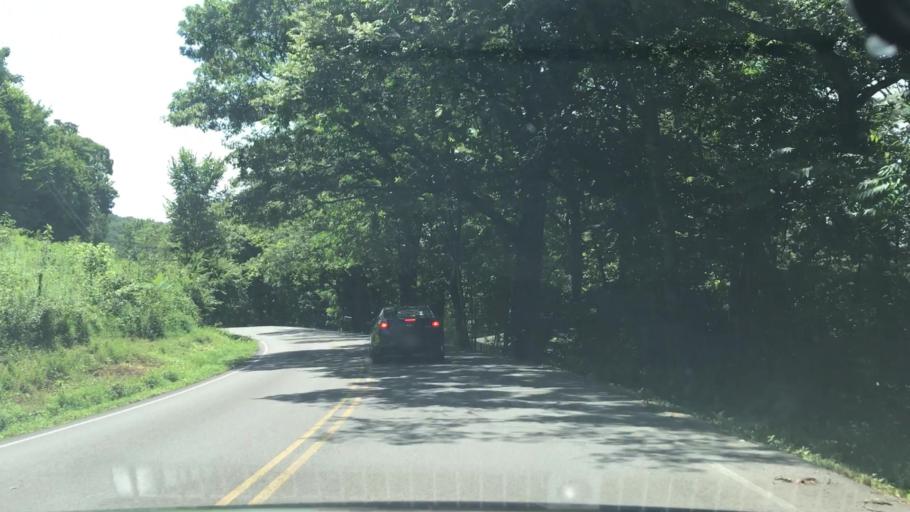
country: US
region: Tennessee
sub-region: Williamson County
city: Franklin
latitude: 35.9650
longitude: -86.8588
